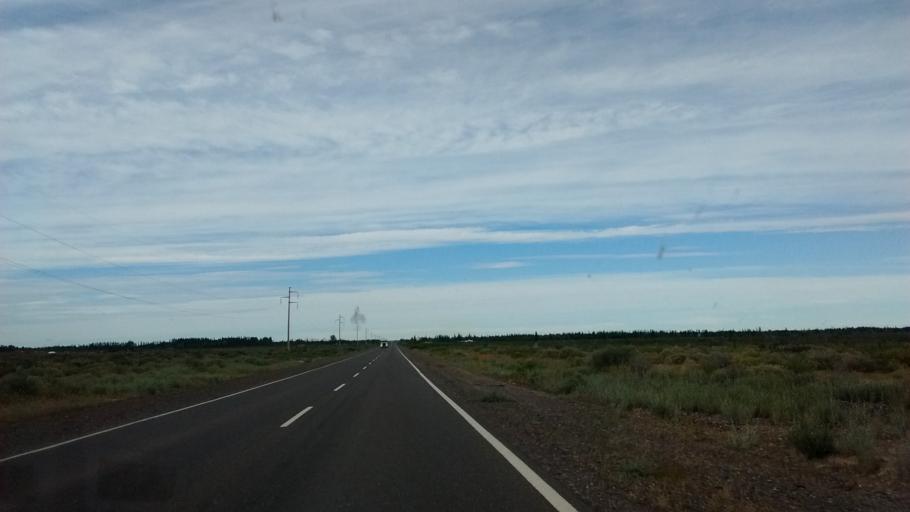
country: AR
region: Rio Negro
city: Contraalmirante Cordero
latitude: -38.6521
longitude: -68.1391
